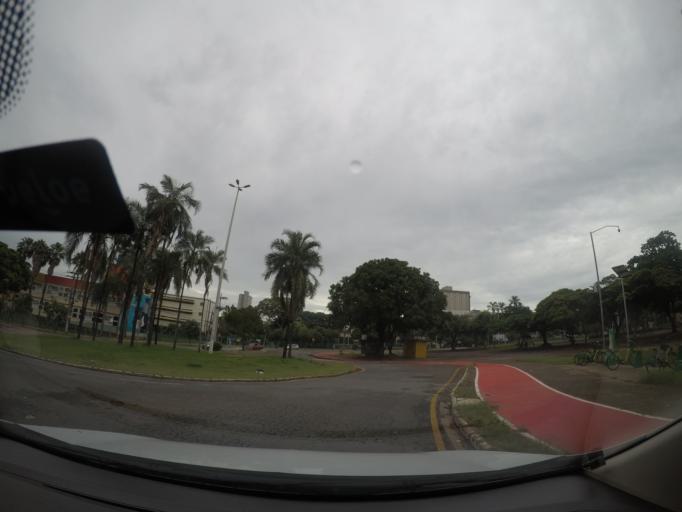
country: BR
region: Goias
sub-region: Goiania
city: Goiania
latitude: -16.6777
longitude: -49.2454
